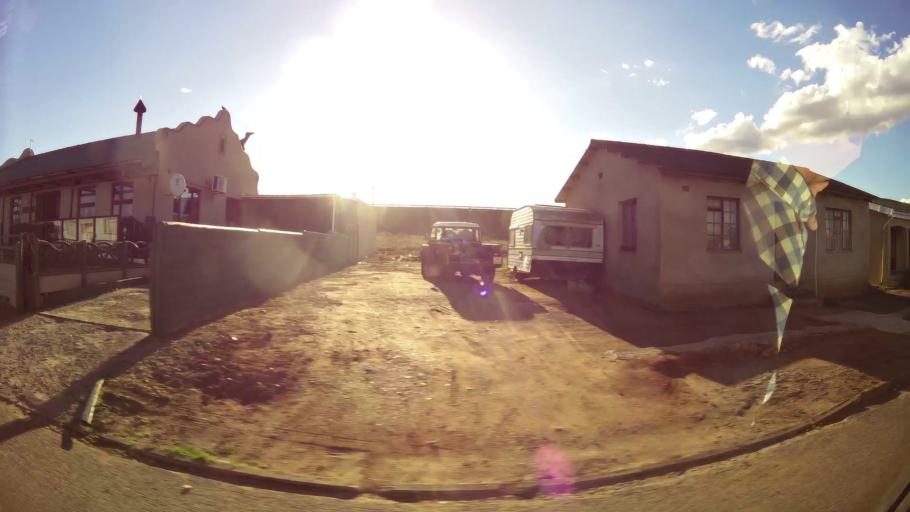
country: ZA
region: Western Cape
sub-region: Eden District Municipality
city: Riversdale
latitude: -34.1037
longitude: 20.9601
